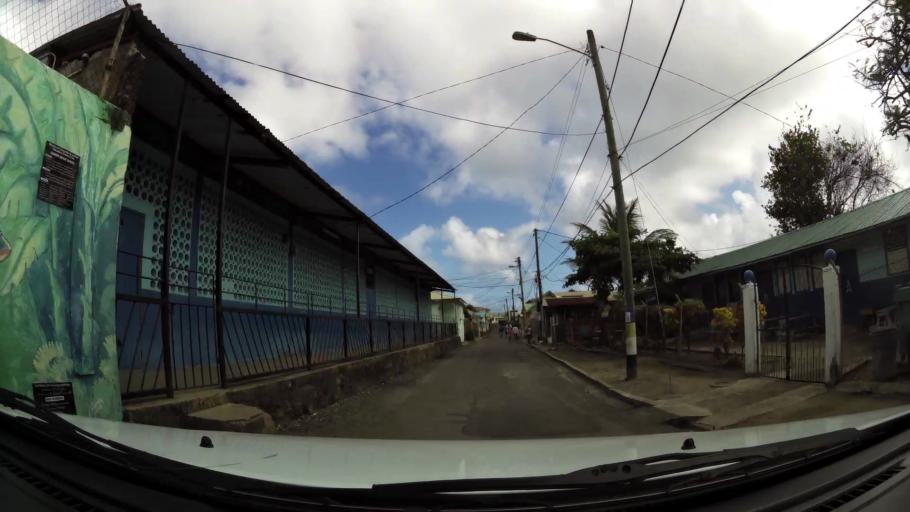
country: LC
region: Dennery Quarter
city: Dennery
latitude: 13.9113
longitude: -60.8907
